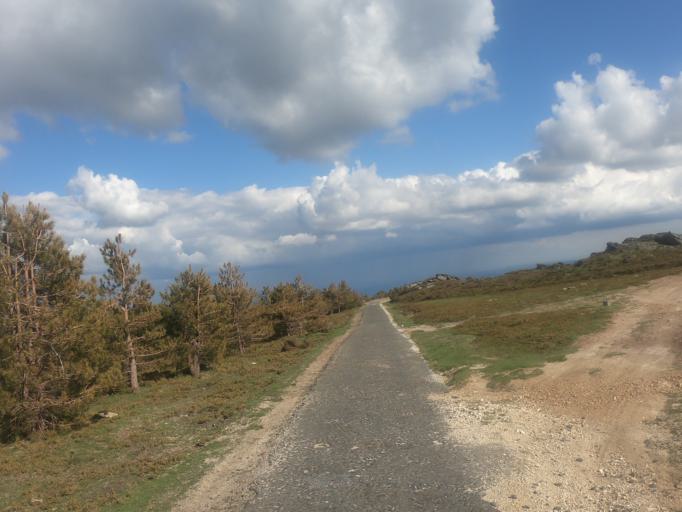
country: PT
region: Vila Real
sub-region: Mesao Frio
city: Mesao Frio
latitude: 41.2470
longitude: -7.8816
